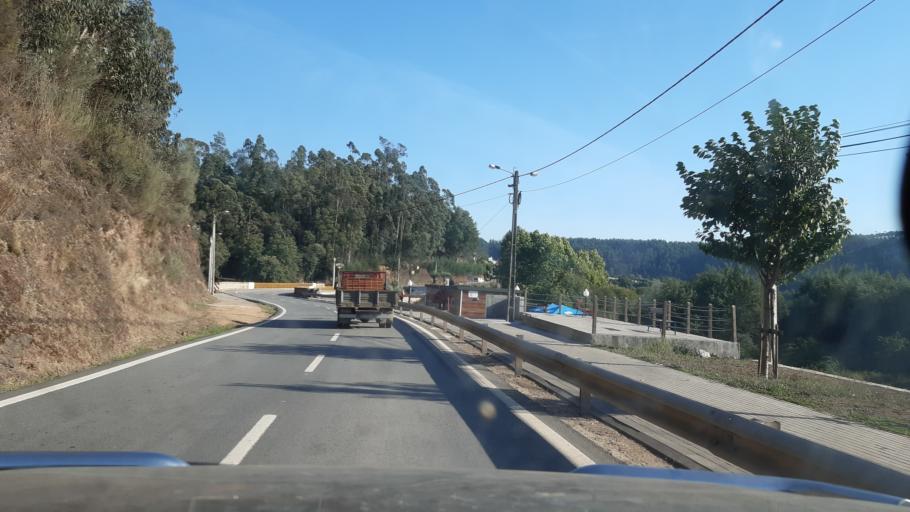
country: PT
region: Aveiro
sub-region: Agueda
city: Agueda
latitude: 40.5668
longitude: -8.4004
